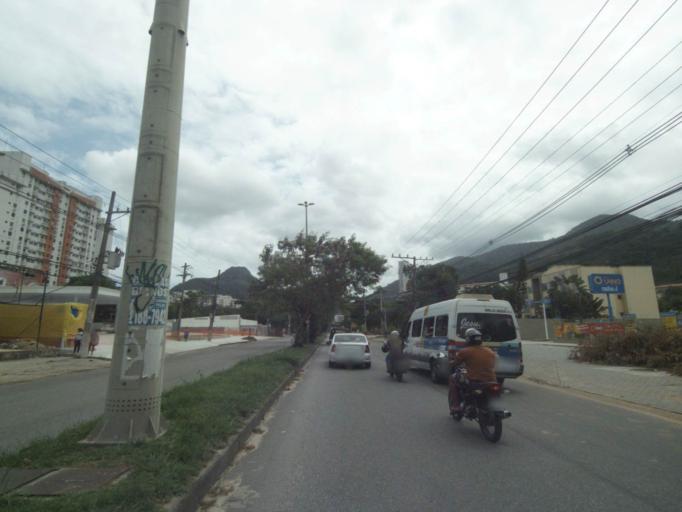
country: BR
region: Rio de Janeiro
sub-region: Nilopolis
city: Nilopolis
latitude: -22.9653
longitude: -43.4080
